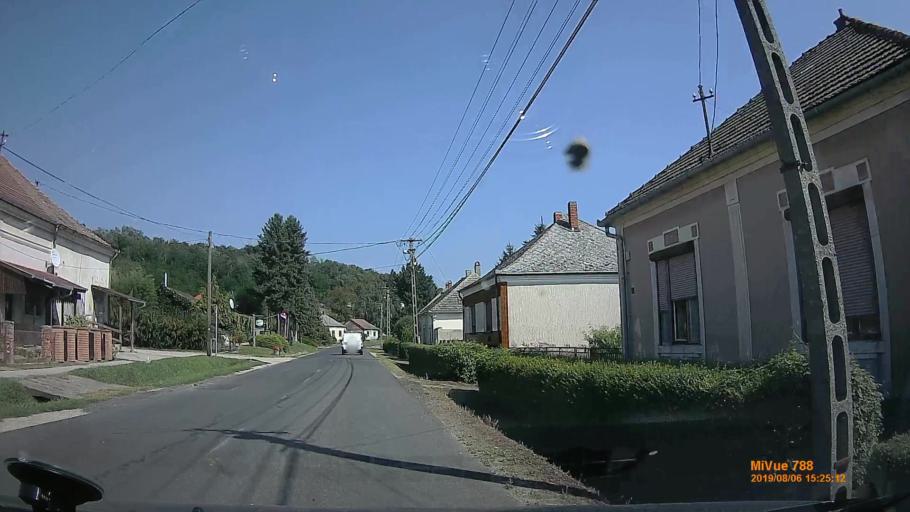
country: HR
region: Koprivnicko-Krizevacka
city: Drnje
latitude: 46.2552
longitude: 16.9432
